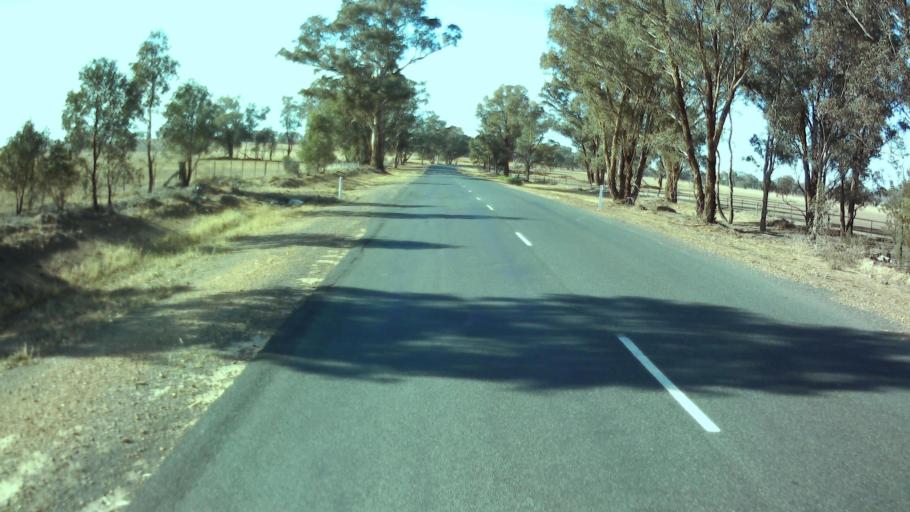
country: AU
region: New South Wales
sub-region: Weddin
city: Grenfell
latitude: -33.9320
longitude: 148.1375
